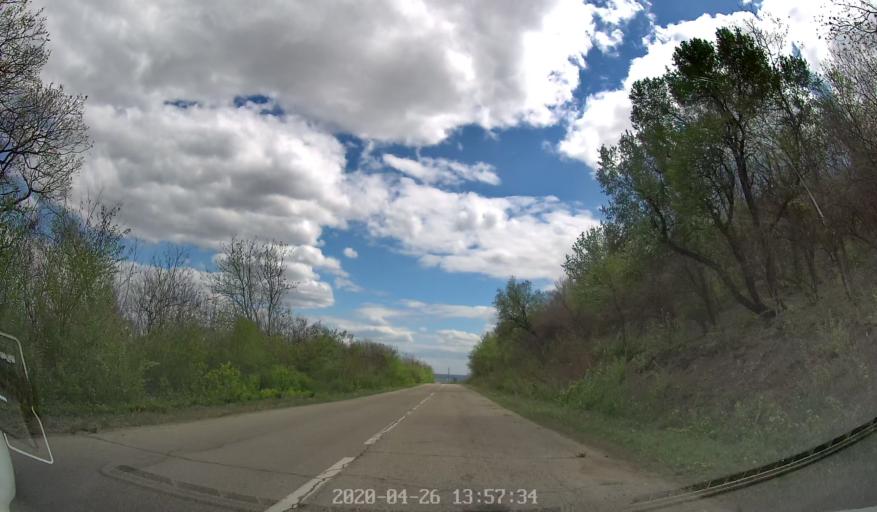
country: MD
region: Telenesti
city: Cocieri
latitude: 47.2735
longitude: 29.1169
